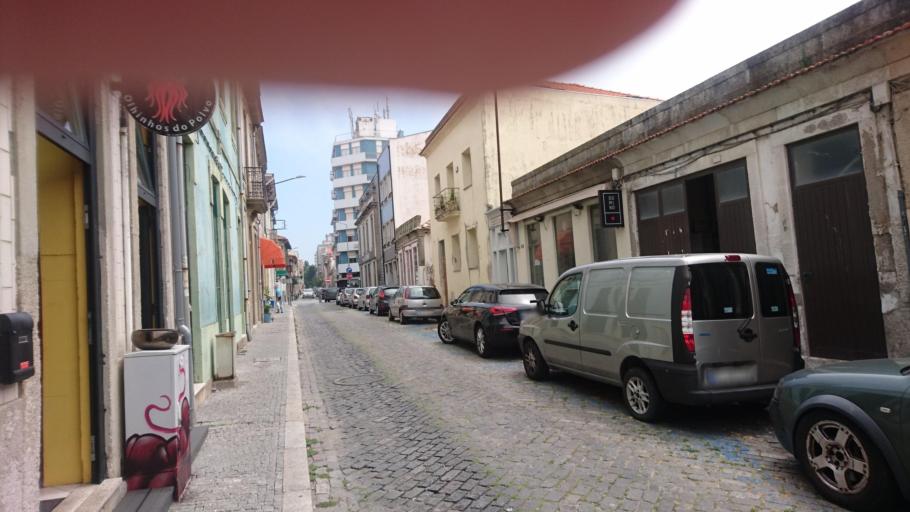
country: PT
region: Porto
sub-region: Matosinhos
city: Leca da Palmeira
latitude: 41.1847
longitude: -8.6961
